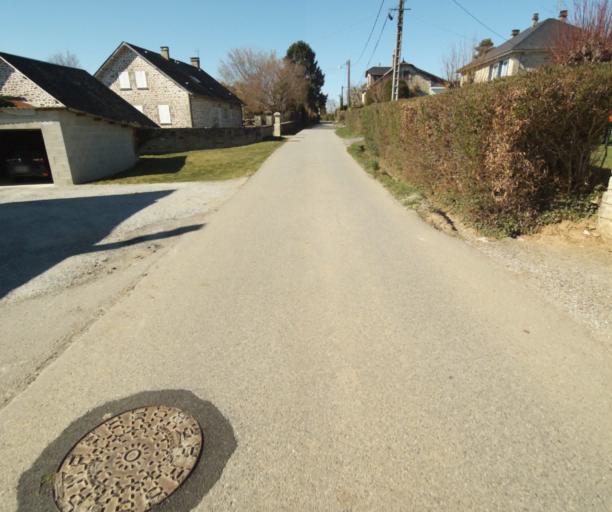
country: FR
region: Limousin
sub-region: Departement de la Correze
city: Chamboulive
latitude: 45.4699
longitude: 1.7362
